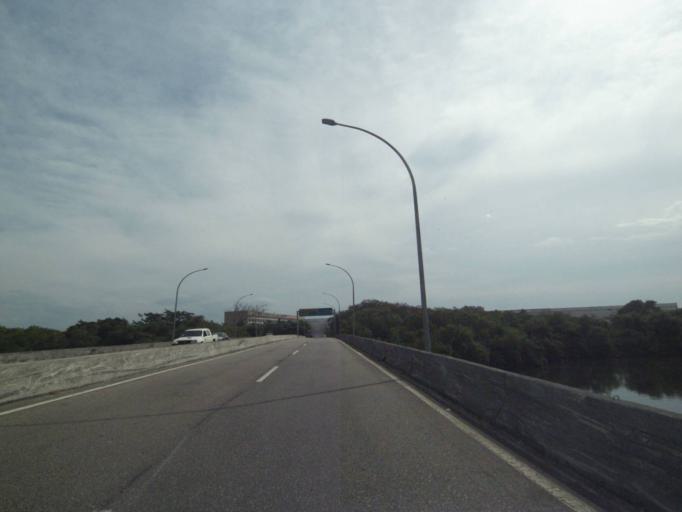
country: BR
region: Rio de Janeiro
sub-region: Rio De Janeiro
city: Rio de Janeiro
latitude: -22.8633
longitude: -43.2337
